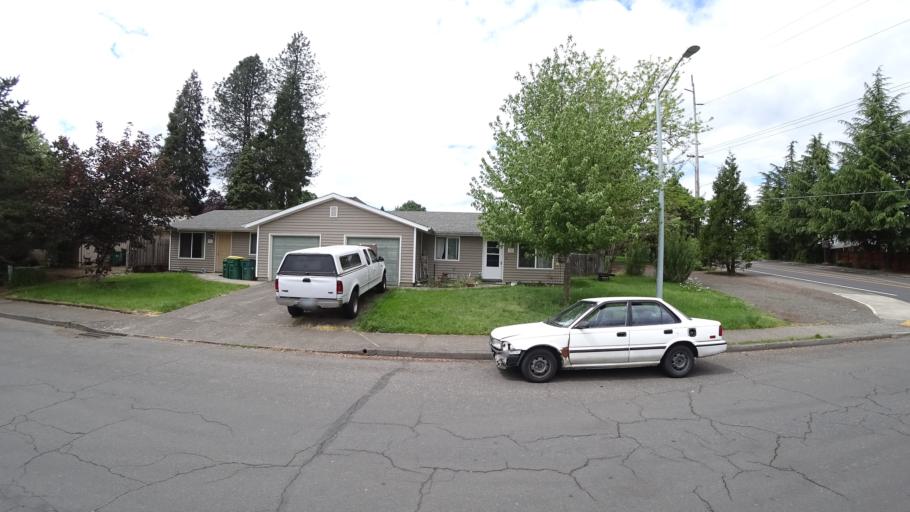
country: US
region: Oregon
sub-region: Washington County
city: Aloha
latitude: 45.4654
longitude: -122.8461
